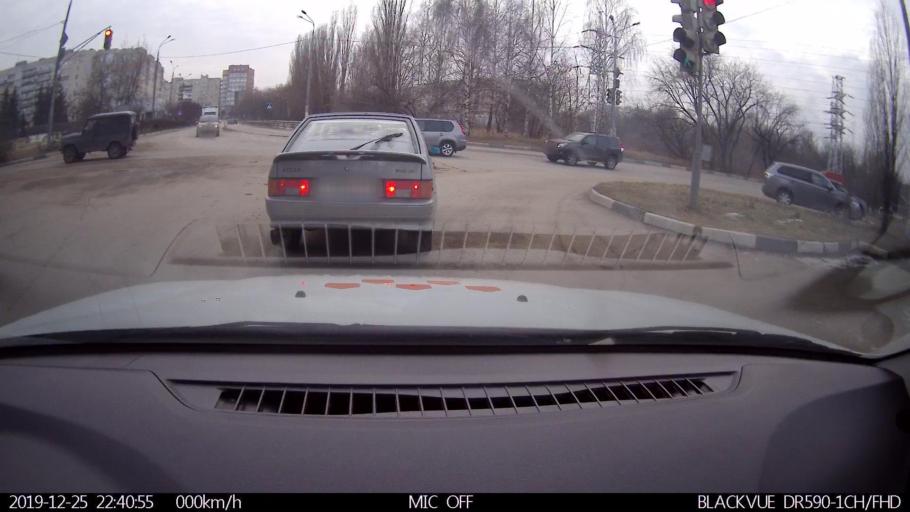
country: RU
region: Nizjnij Novgorod
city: Nizhniy Novgorod
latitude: 56.3306
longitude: 43.8714
